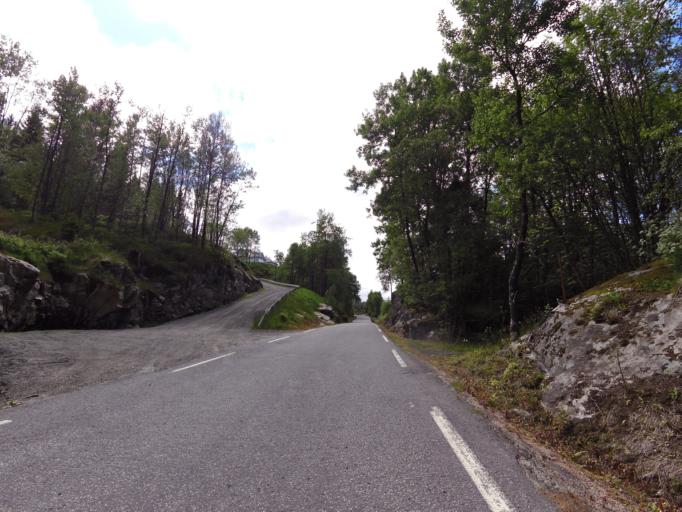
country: NO
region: Vest-Agder
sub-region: Kvinesdal
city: Liknes
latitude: 58.2854
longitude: 6.9321
